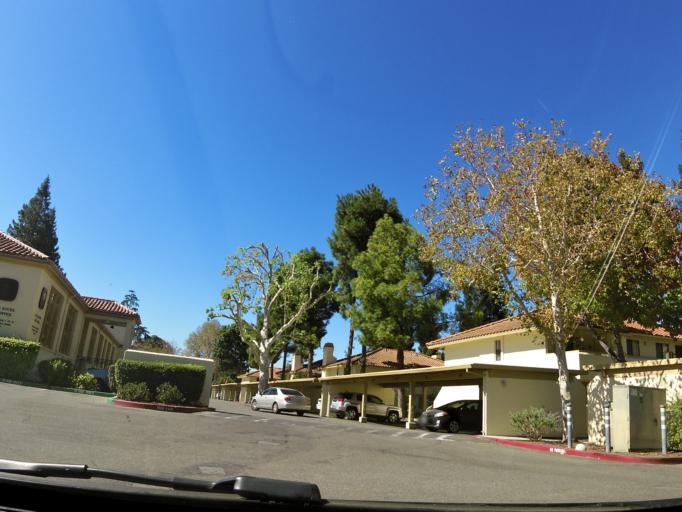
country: US
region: California
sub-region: Santa Clara County
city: Campbell
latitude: 37.2882
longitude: -121.9481
